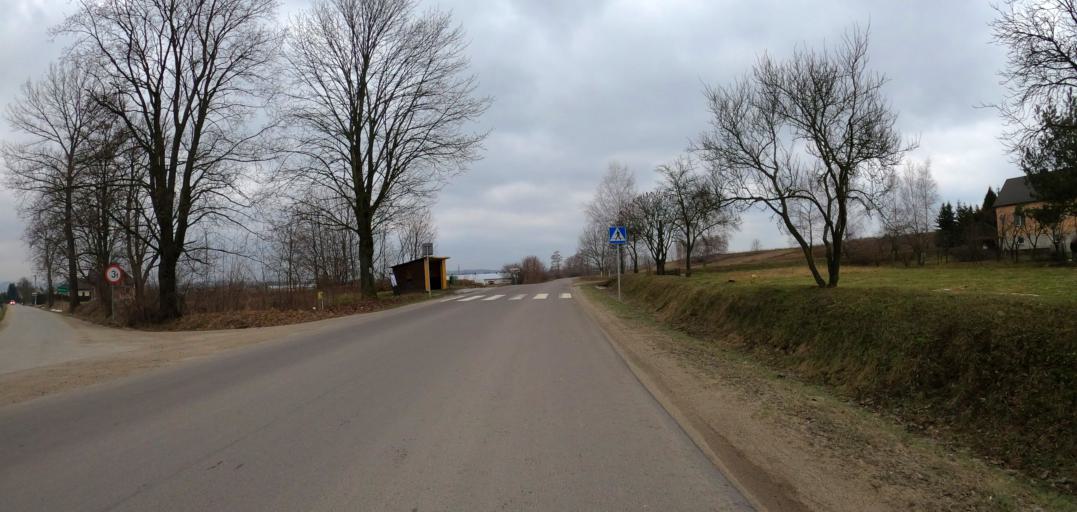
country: PL
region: Subcarpathian Voivodeship
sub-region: Powiat debicki
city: Pilzno
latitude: 49.9807
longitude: 21.3330
